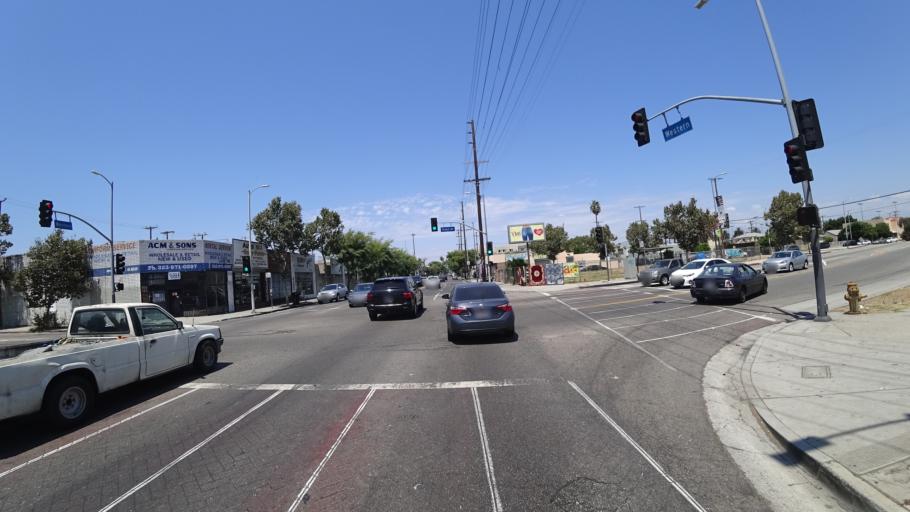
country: US
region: California
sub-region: Los Angeles County
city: Westmont
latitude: 33.9817
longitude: -118.3089
